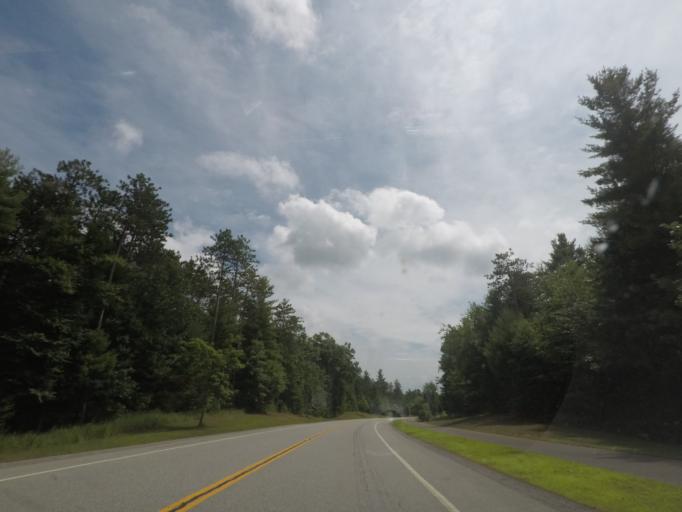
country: US
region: New York
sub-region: Saratoga County
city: Country Knolls
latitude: 42.9607
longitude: -73.7610
